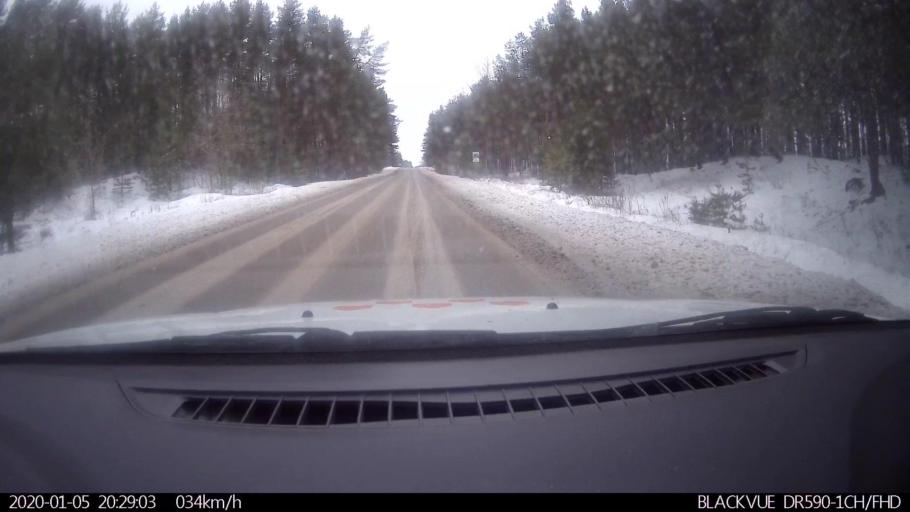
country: RU
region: Nizjnij Novgorod
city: Lukino
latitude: 56.3922
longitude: 43.7379
